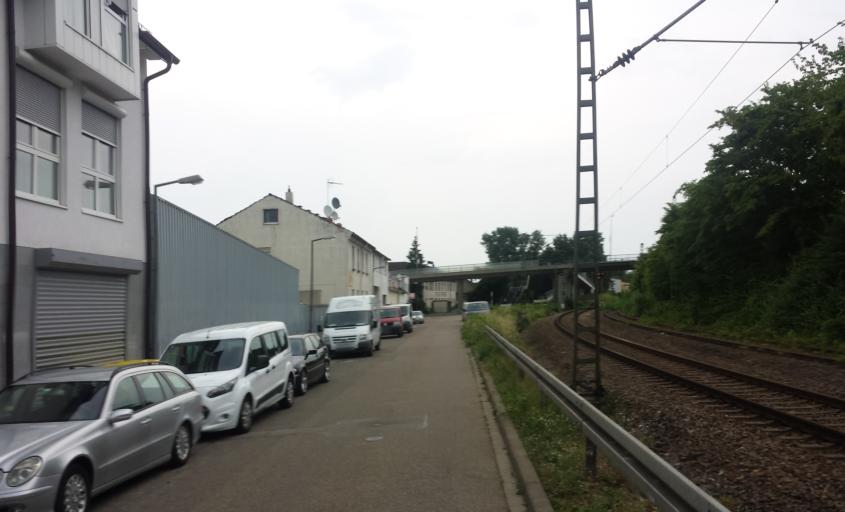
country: DE
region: Rheinland-Pfalz
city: Altrip
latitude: 49.4610
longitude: 8.4949
